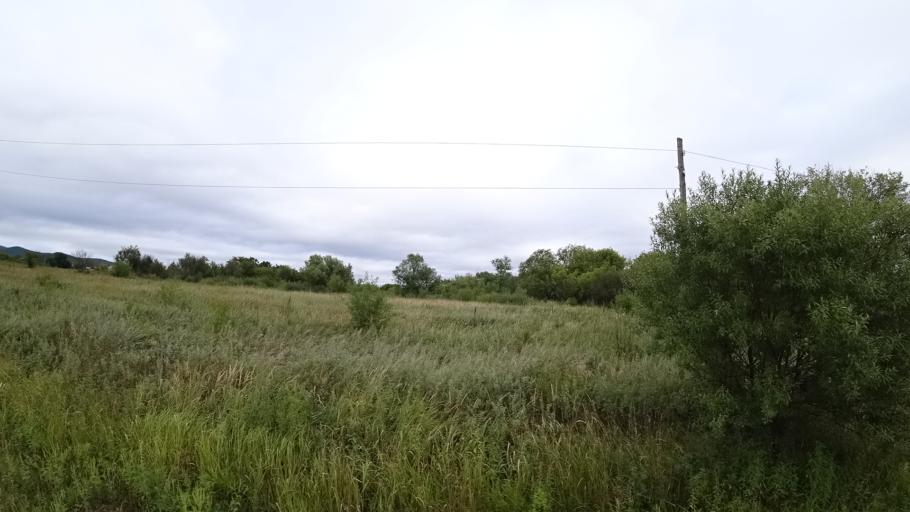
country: RU
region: Primorskiy
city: Rettikhovka
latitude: 44.1297
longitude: 132.6353
